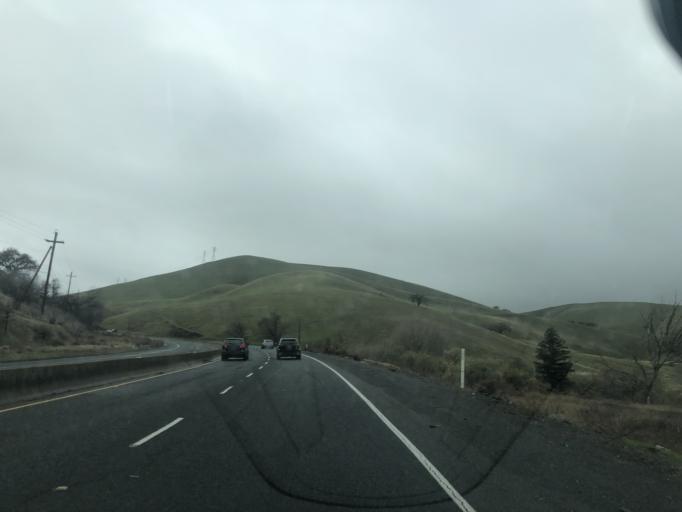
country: US
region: California
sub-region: Contra Costa County
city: Clayton
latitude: 37.9749
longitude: -121.9129
